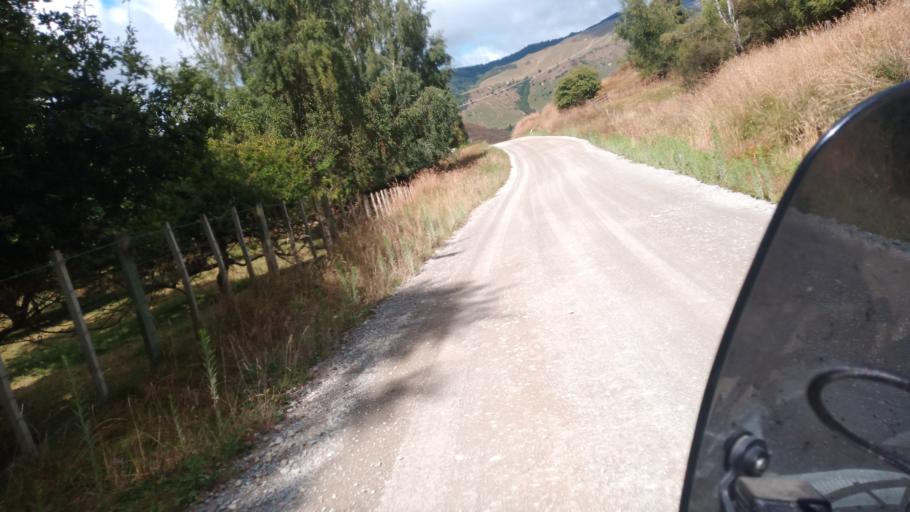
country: NZ
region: Hawke's Bay
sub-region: Wairoa District
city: Wairoa
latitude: -38.6095
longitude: 177.4462
